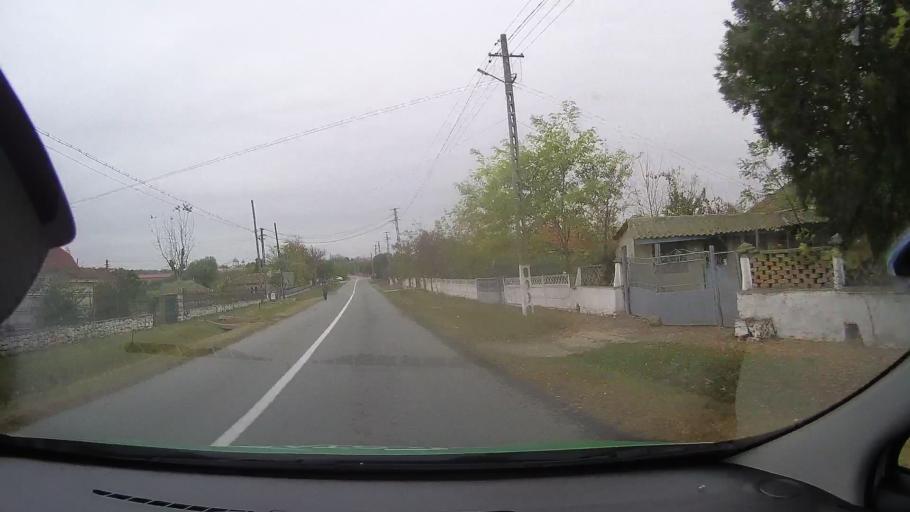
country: RO
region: Constanta
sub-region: Comuna Targusor
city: Targusor
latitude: 44.4638
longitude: 28.4232
